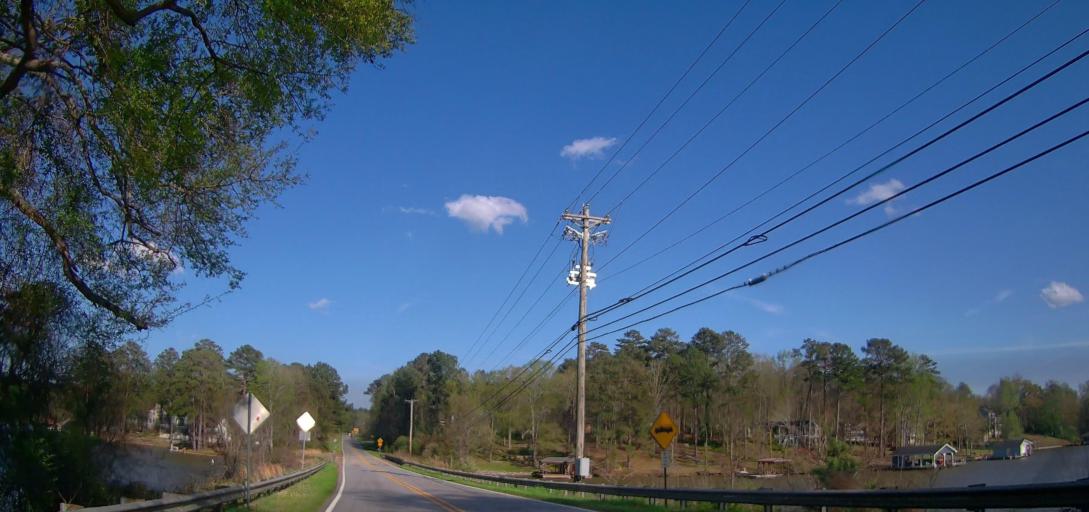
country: US
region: Georgia
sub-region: Putnam County
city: Eatonton
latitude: 33.2035
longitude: -83.3790
